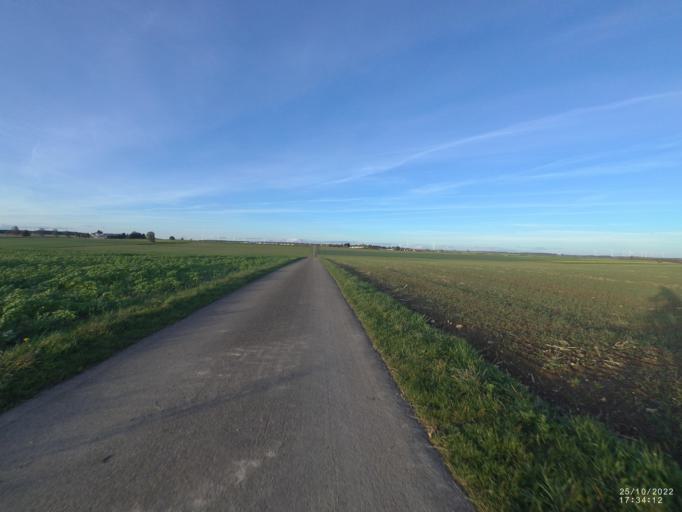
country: DE
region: Baden-Wuerttemberg
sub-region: Regierungsbezirk Stuttgart
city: Bohmenkirch
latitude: 48.6655
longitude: 9.9217
